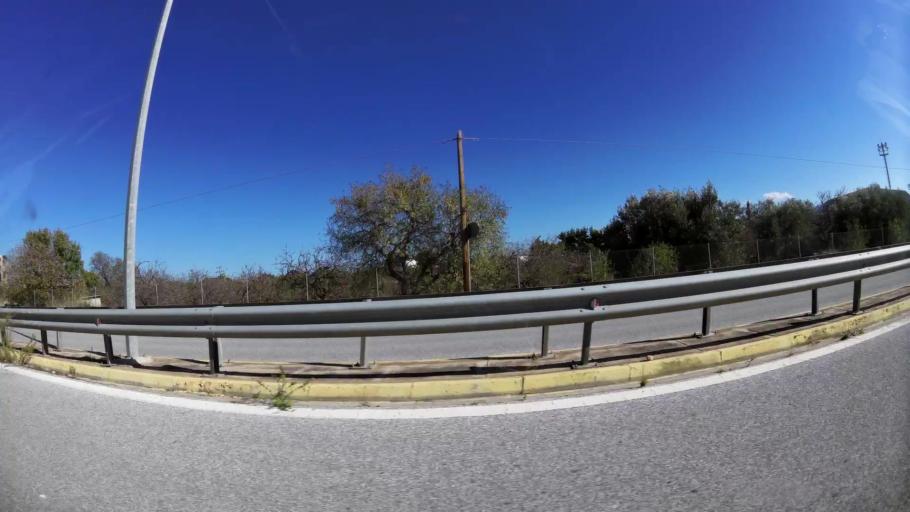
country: GR
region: Attica
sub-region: Nomarchia Anatolikis Attikis
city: Pallini
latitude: 37.9978
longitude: 23.8910
